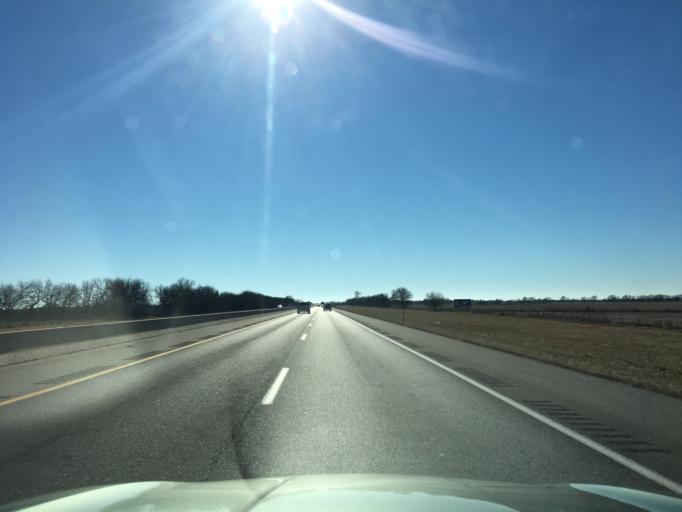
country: US
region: Kansas
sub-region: Sumner County
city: Wellington
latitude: 37.1027
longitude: -97.3388
